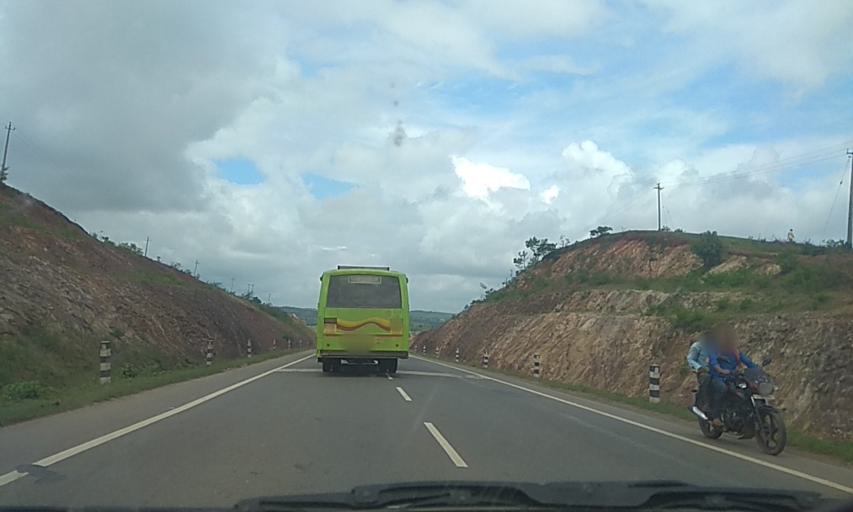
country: IN
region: Karnataka
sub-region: Dharwad
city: Hubli
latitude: 15.4016
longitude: 74.9969
